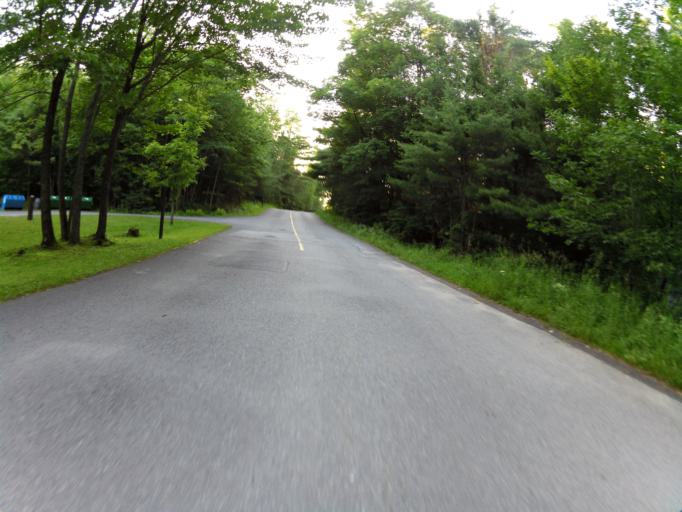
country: CA
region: Quebec
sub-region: Outaouais
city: Wakefield
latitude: 45.6016
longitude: -76.0072
